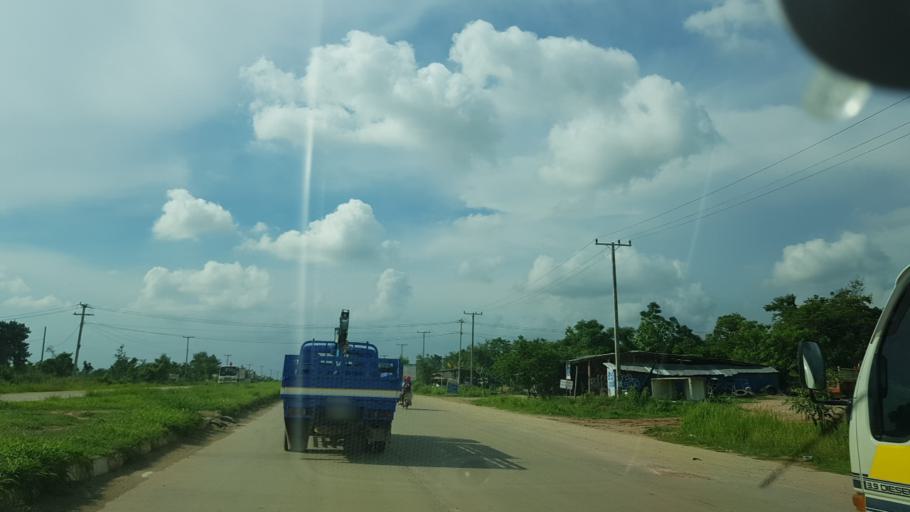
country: TH
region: Nong Khai
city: Nong Khai
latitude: 17.9110
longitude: 102.7200
